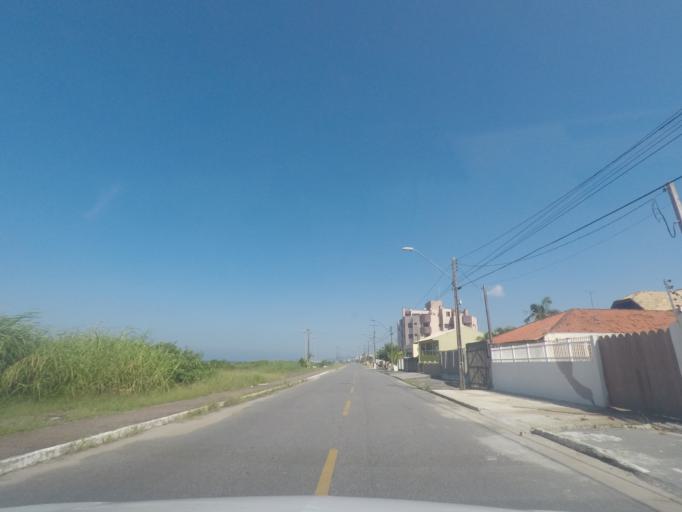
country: BR
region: Parana
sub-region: Pontal Do Parana
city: Pontal do Parana
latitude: -25.7560
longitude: -48.5038
